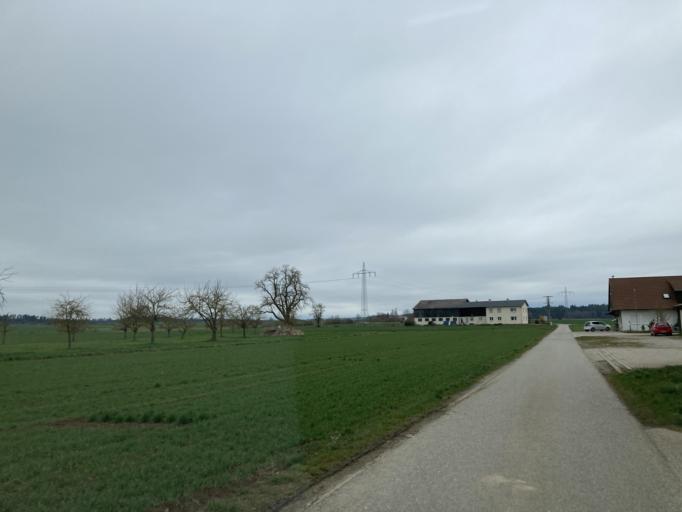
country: DE
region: Baden-Wuerttemberg
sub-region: Regierungsbezirk Stuttgart
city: Motzingen
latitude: 48.4993
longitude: 8.7978
